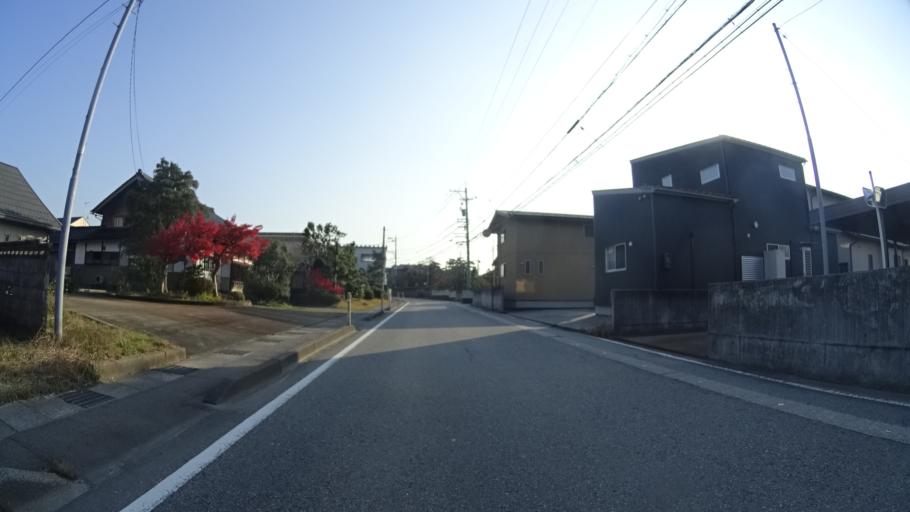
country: JP
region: Toyama
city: Toyama-shi
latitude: 36.6877
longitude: 137.2710
